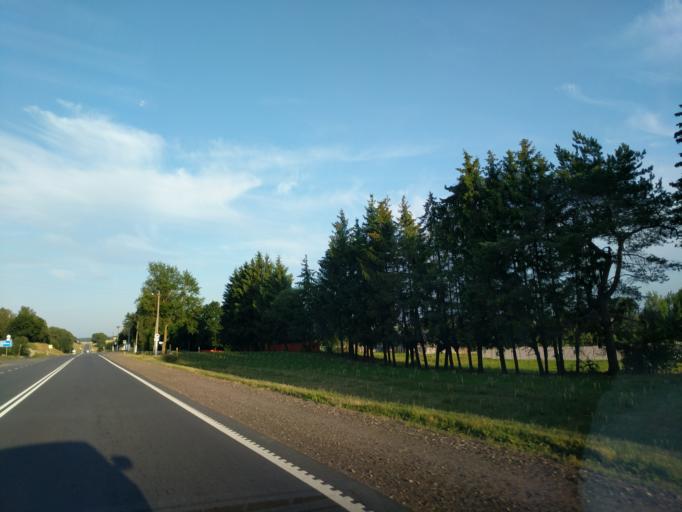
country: BY
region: Minsk
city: Syomkava
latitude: 54.1085
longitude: 27.4599
